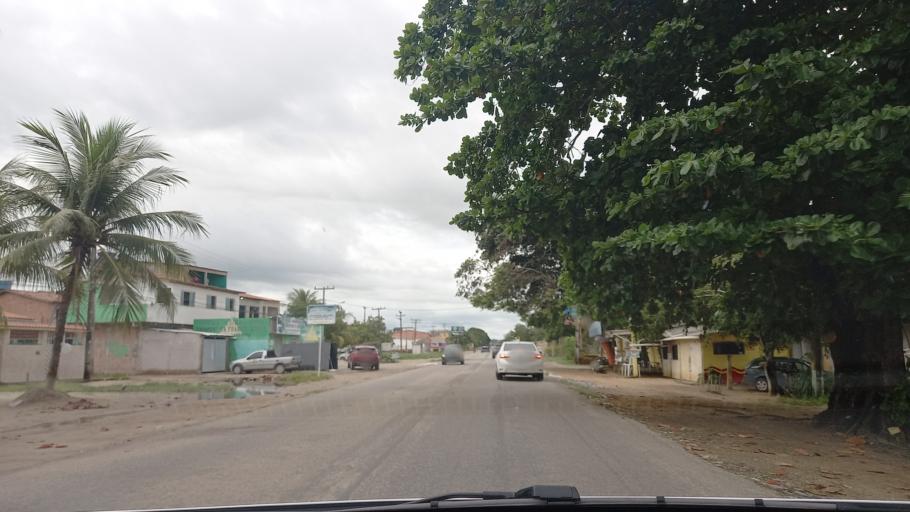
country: BR
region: Pernambuco
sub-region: Sao Jose Da Coroa Grande
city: Sao Jose da Coroa Grande
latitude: -8.9046
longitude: -35.1517
